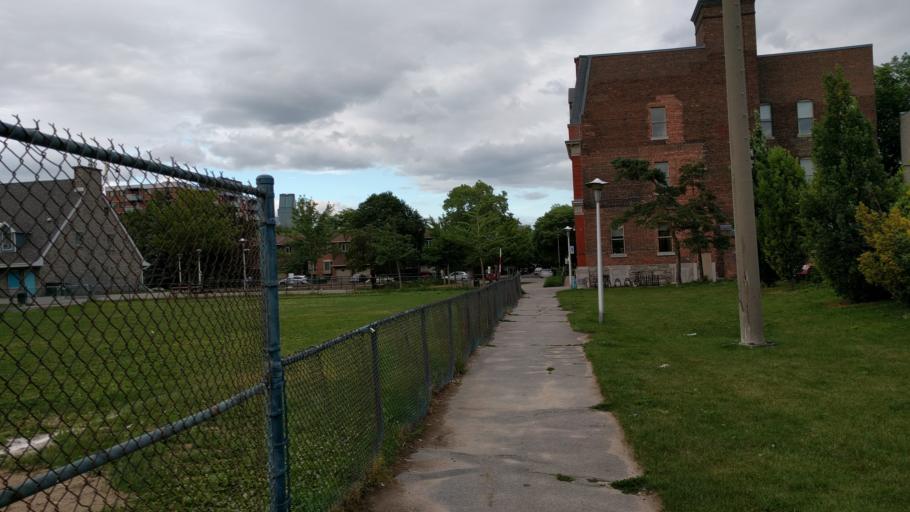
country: CA
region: Quebec
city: Westmount
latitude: 45.4833
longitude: -73.5757
